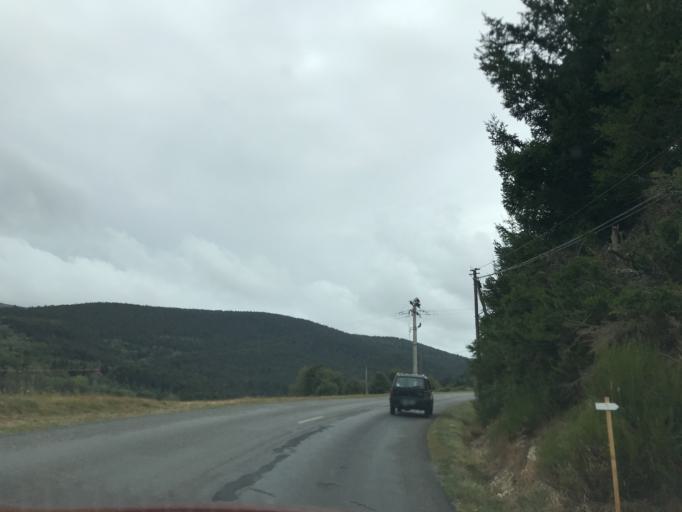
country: FR
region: Auvergne
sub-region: Departement du Puy-de-Dome
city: Job
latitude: 45.6904
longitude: 3.8355
